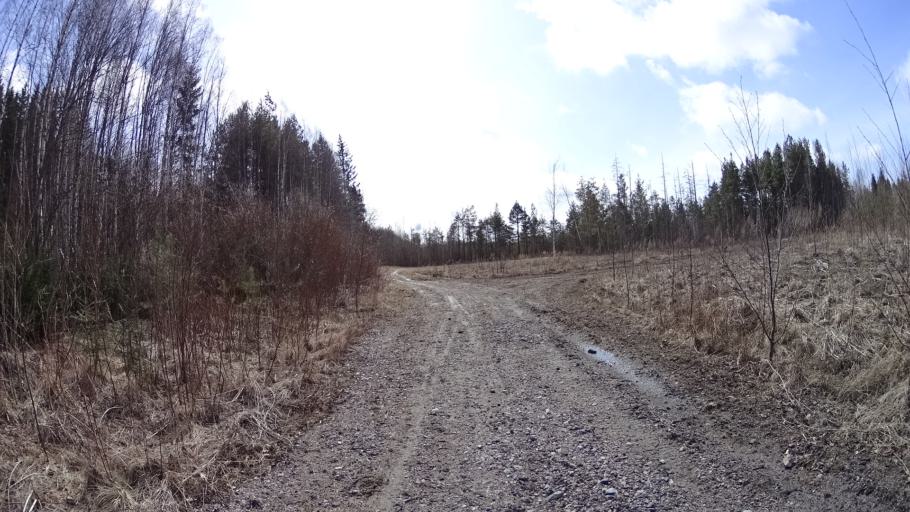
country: FI
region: Uusimaa
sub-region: Helsinki
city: Kilo
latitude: 60.3226
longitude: 24.8223
